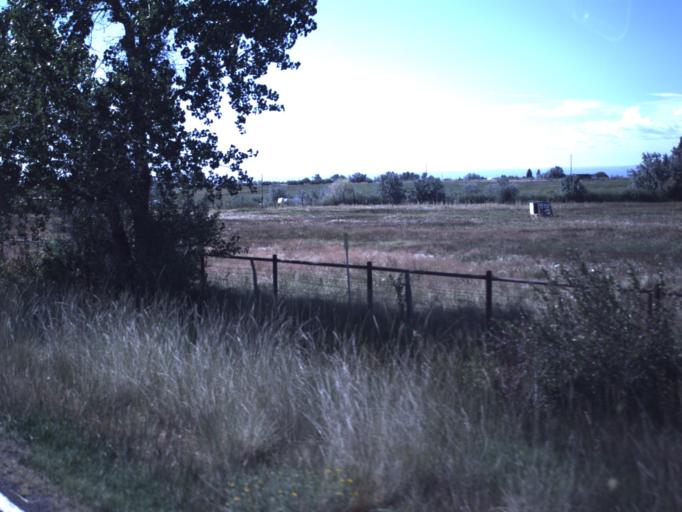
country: US
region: Utah
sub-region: Duchesne County
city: Duchesne
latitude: 40.3065
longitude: -110.2425
